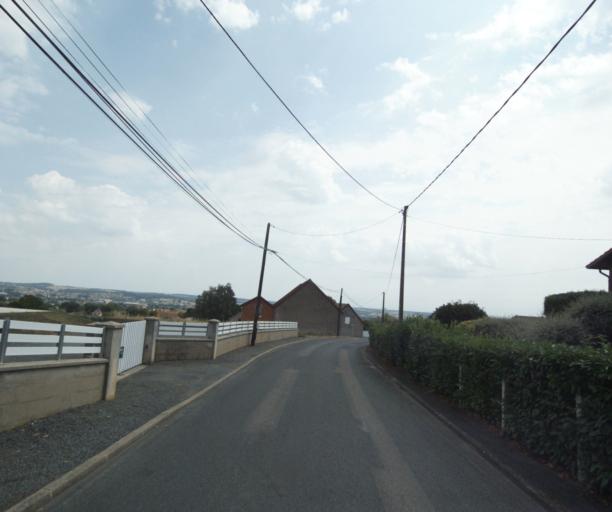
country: FR
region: Bourgogne
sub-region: Departement de Saone-et-Loire
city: Gueugnon
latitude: 46.6008
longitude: 4.0211
